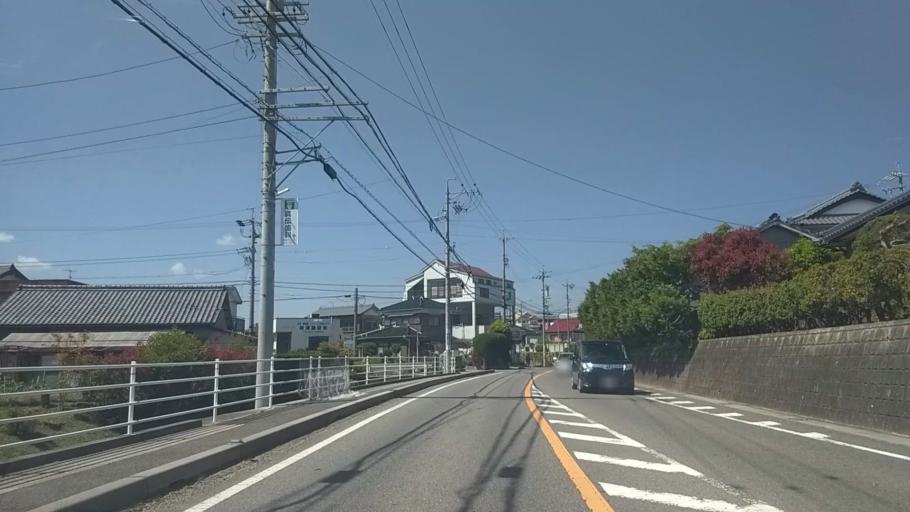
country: JP
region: Aichi
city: Okazaki
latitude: 34.9762
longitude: 137.1854
